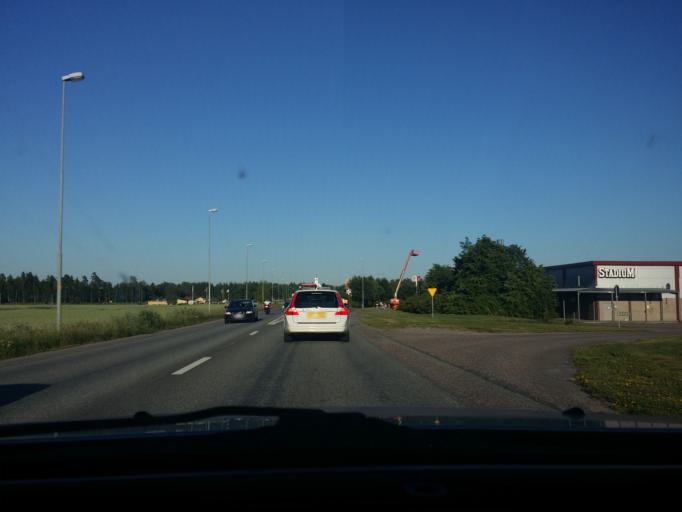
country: SE
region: Vaestmanland
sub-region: Vasteras
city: Hokasen
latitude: 59.6114
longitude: 16.6188
